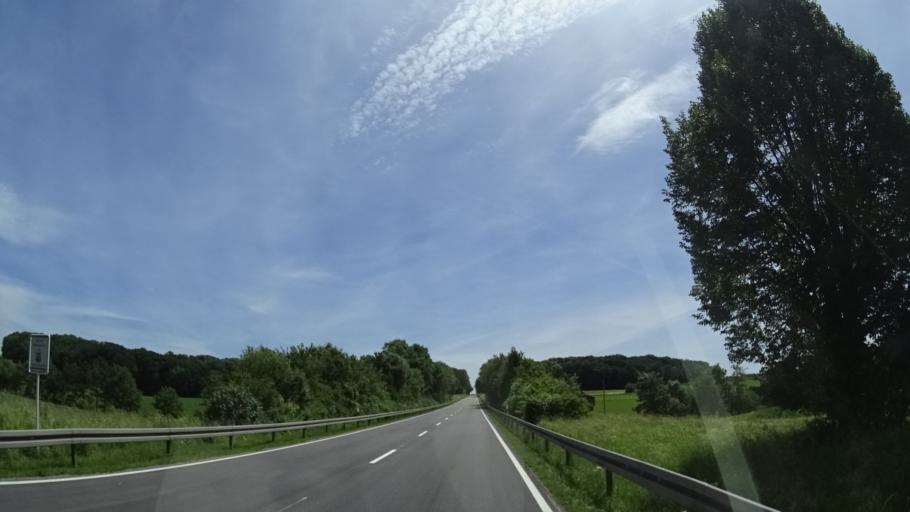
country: DE
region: Baden-Wuerttemberg
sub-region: Regierungsbezirk Stuttgart
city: Kupferzell
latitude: 49.1902
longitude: 9.6954
